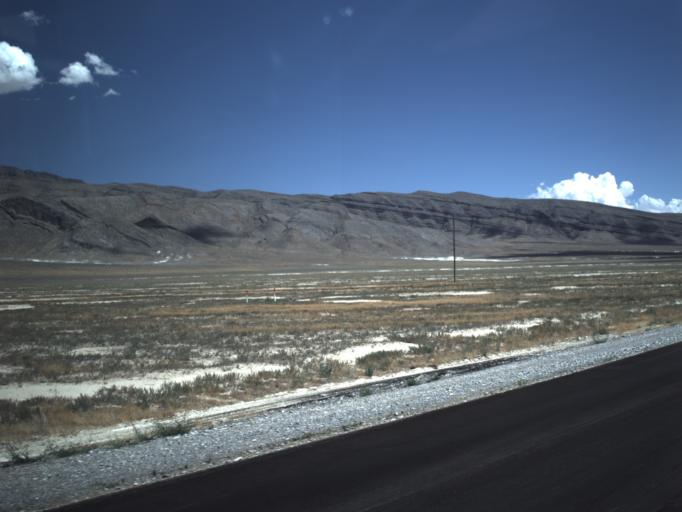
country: US
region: Utah
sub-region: Beaver County
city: Milford
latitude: 39.0689
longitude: -113.4575
